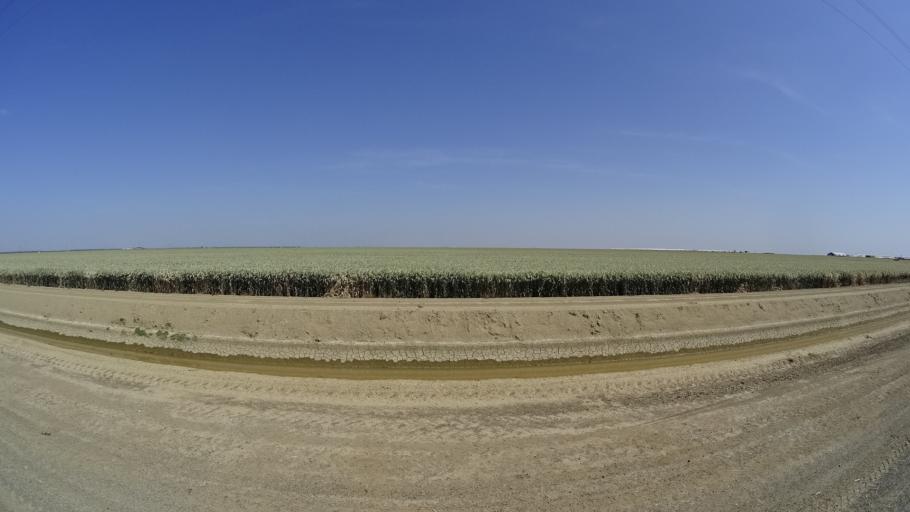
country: US
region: California
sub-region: Kings County
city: Kettleman City
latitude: 36.0941
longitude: -119.9439
